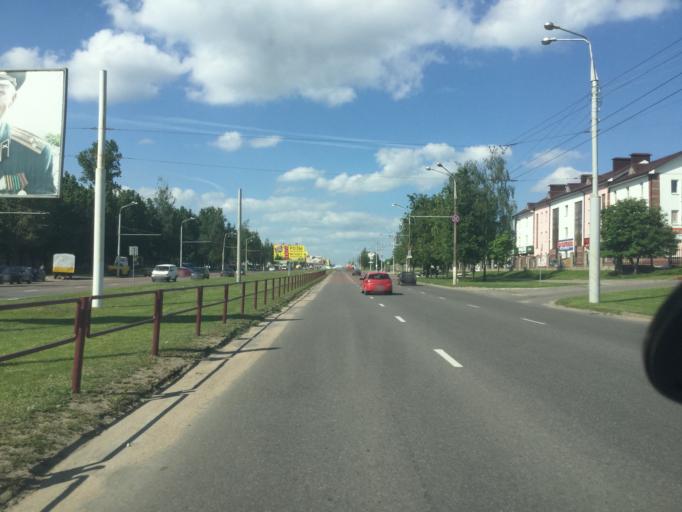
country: BY
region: Vitebsk
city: Vitebsk
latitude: 55.1772
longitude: 30.2455
